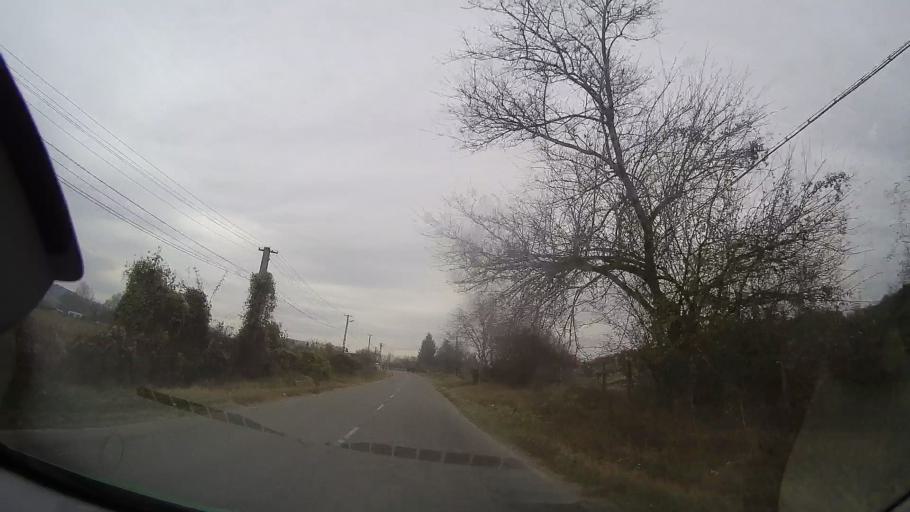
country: RO
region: Prahova
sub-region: Comuna Iordachianu
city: Iordacheanu
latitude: 45.0270
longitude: 26.2390
